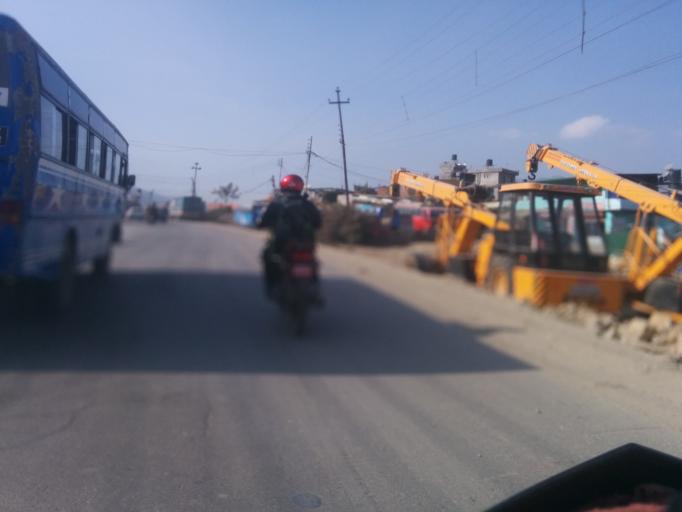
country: NP
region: Central Region
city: Kirtipur
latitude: 27.6874
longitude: 85.2909
